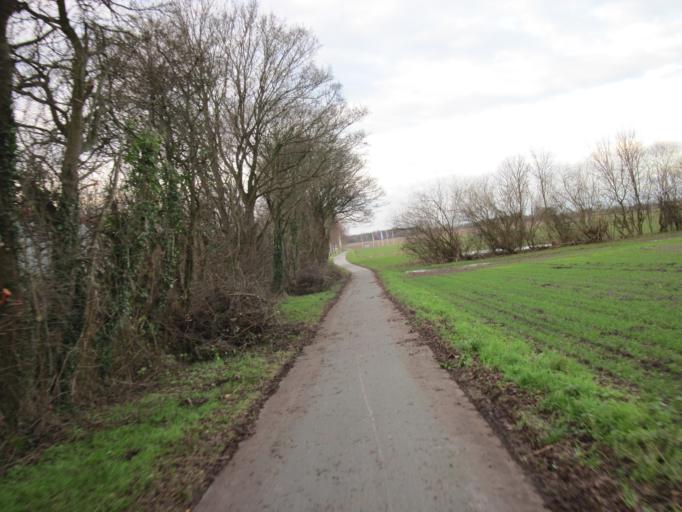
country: DE
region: North Rhine-Westphalia
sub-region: Regierungsbezirk Detmold
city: Paderborn
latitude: 51.6988
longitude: 8.6776
